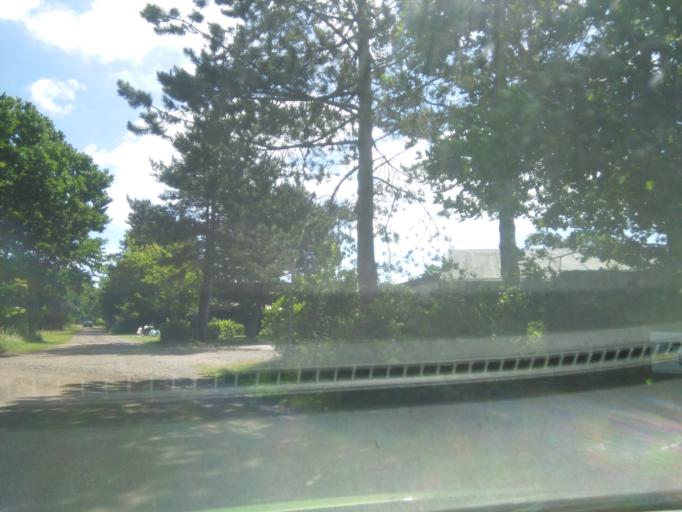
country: DK
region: Central Jutland
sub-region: Arhus Kommune
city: Logten
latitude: 56.1882
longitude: 10.3726
